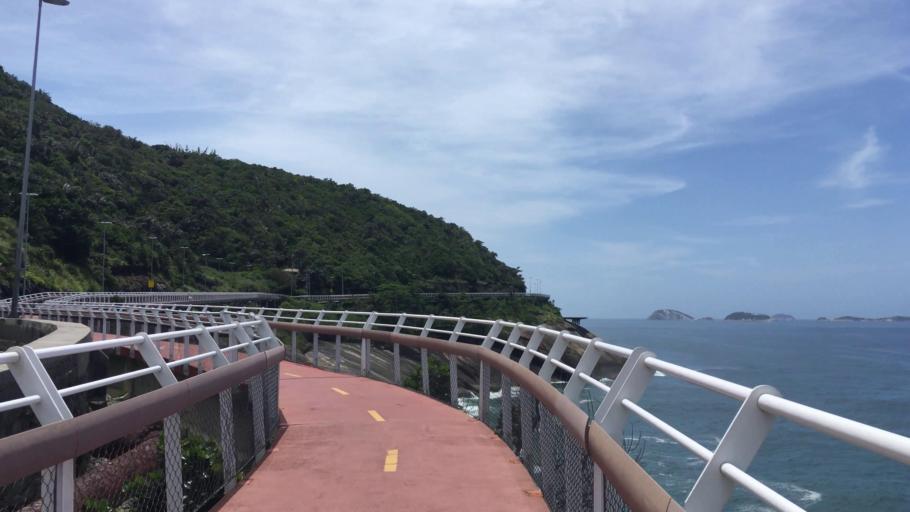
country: BR
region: Rio de Janeiro
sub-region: Rio De Janeiro
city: Rio de Janeiro
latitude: -22.9995
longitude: -43.2486
